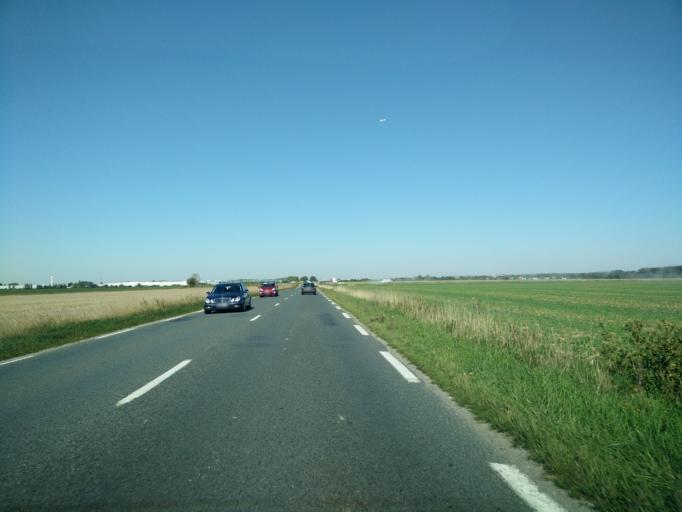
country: FR
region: Ile-de-France
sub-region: Departement de Seine-et-Marne
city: Claye-Souilly
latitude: 48.9738
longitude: 2.6611
